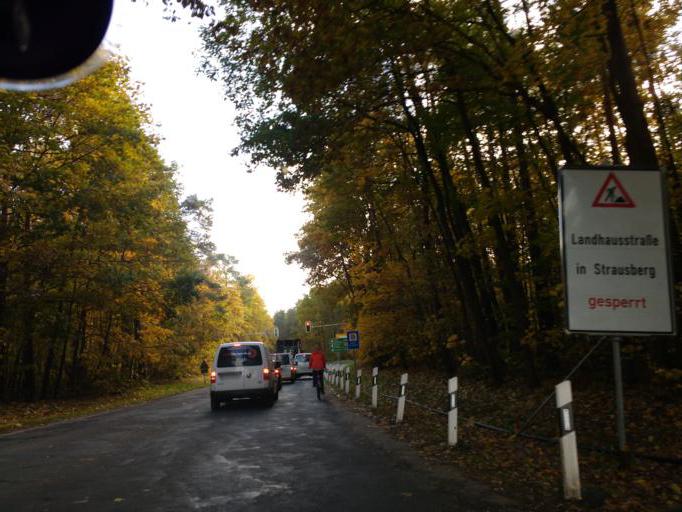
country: DE
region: Brandenburg
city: Strausberg
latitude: 52.5510
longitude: 13.8480
